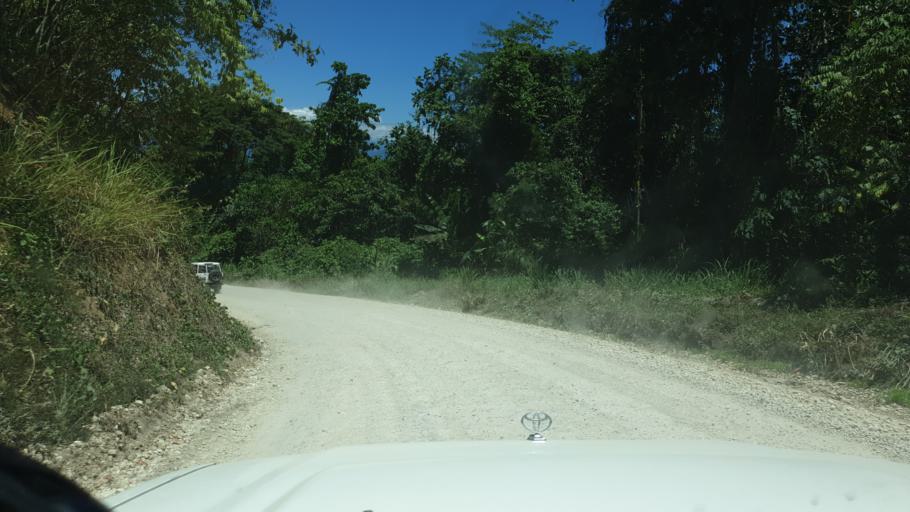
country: PG
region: Madang
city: Madang
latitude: -5.5305
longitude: 145.4109
